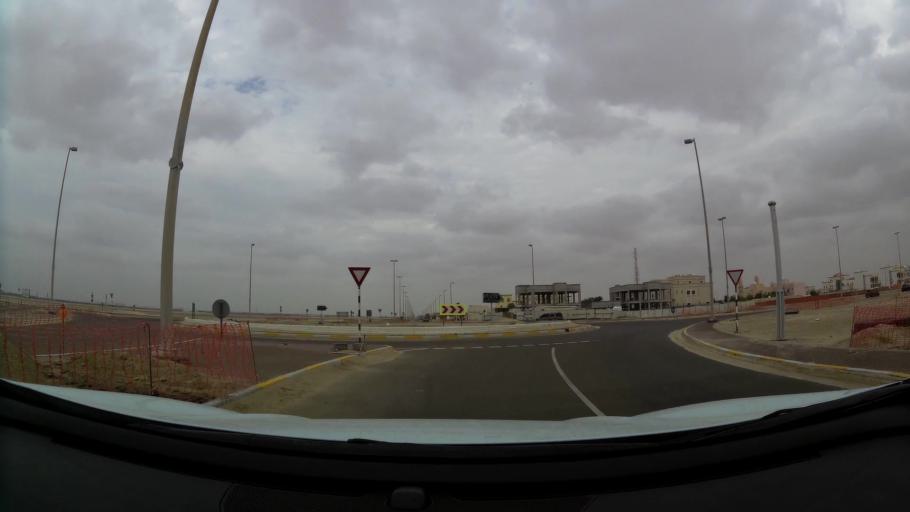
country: AE
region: Abu Dhabi
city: Abu Dhabi
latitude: 24.3825
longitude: 54.6348
